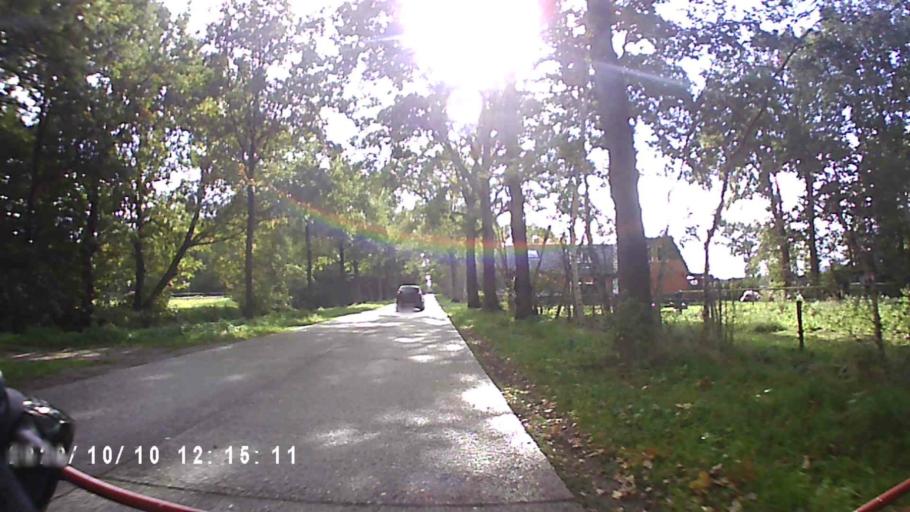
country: NL
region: Friesland
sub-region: Gemeente Heerenveen
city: Jubbega
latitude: 53.0273
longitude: 6.1626
